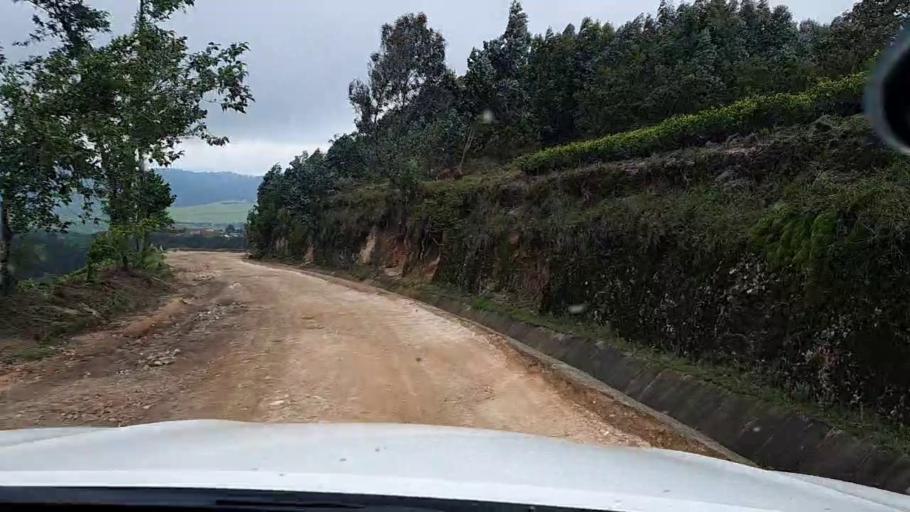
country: RW
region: Western Province
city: Kibuye
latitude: -2.2455
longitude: 29.3461
